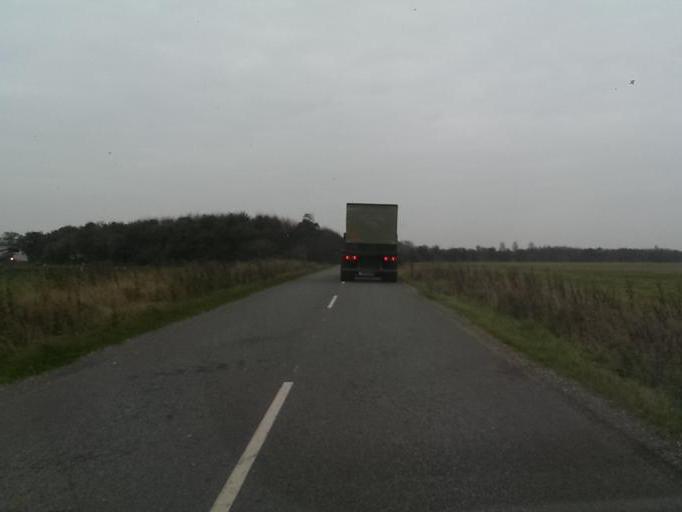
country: DK
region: South Denmark
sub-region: Esbjerg Kommune
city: Tjaereborg
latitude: 55.4994
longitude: 8.5201
